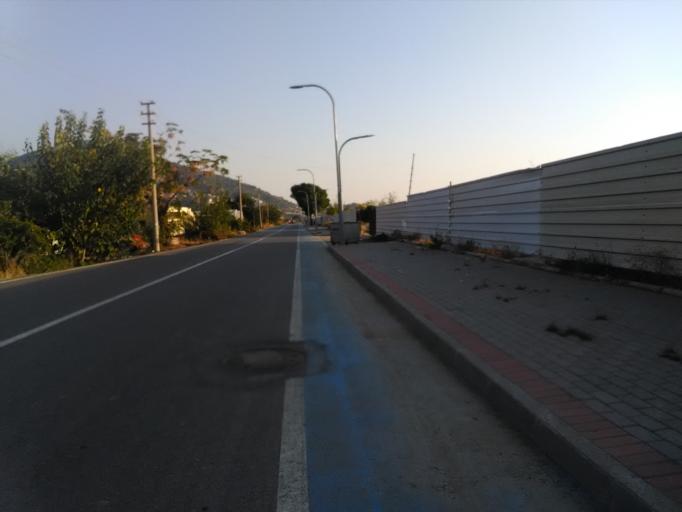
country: TR
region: Antalya
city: Gazipasa
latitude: 36.2525
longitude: 32.2920
